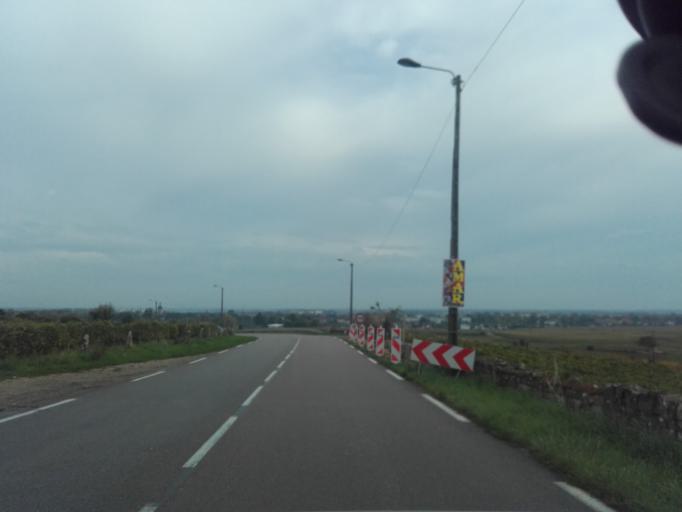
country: FR
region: Bourgogne
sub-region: Departement de la Cote-d'Or
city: Beaune
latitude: 47.0292
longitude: 4.8154
